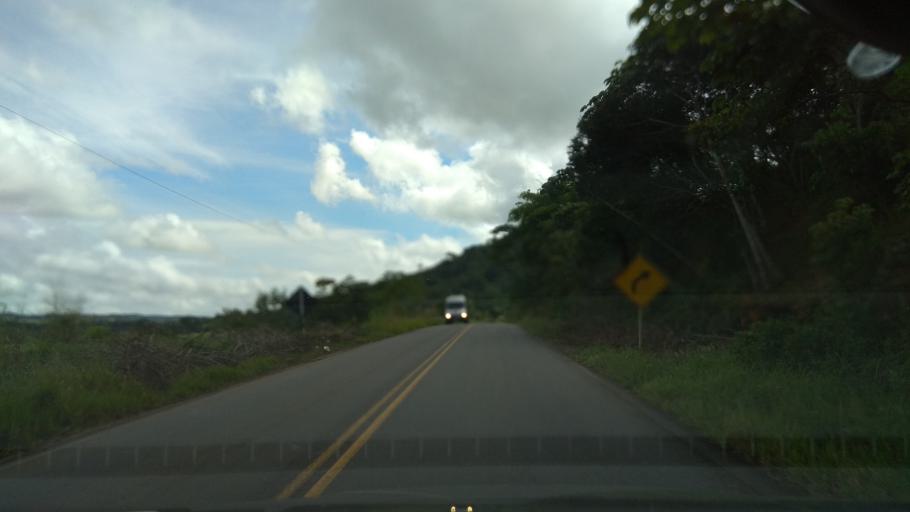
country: BR
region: Bahia
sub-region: Mutuipe
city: Mutuipe
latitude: -13.1876
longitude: -39.4414
